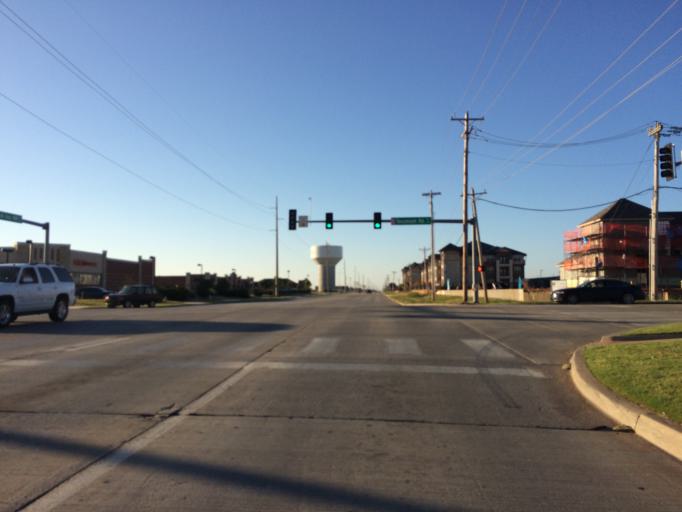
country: US
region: Oklahoma
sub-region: Cleveland County
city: Norman
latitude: 35.2622
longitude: -97.4944
